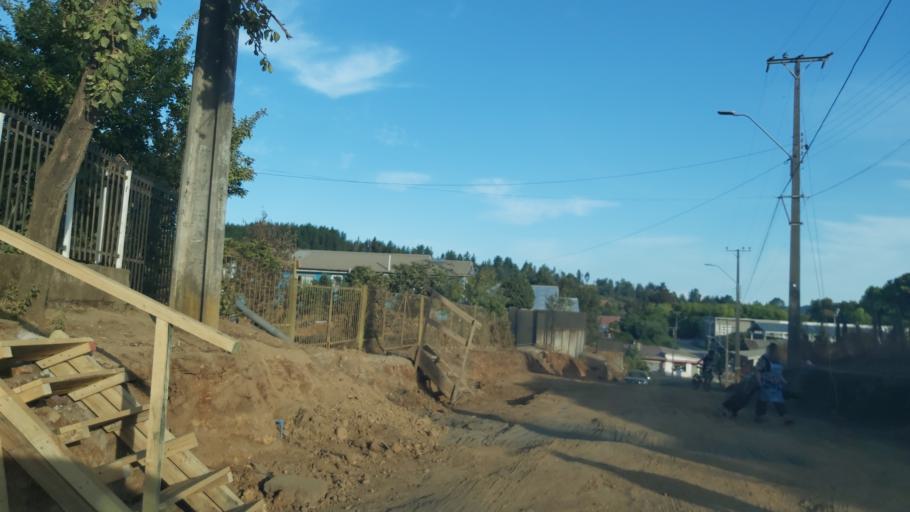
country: CL
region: Biobio
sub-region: Provincia de Biobio
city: La Laja
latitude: -37.1605
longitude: -72.9098
